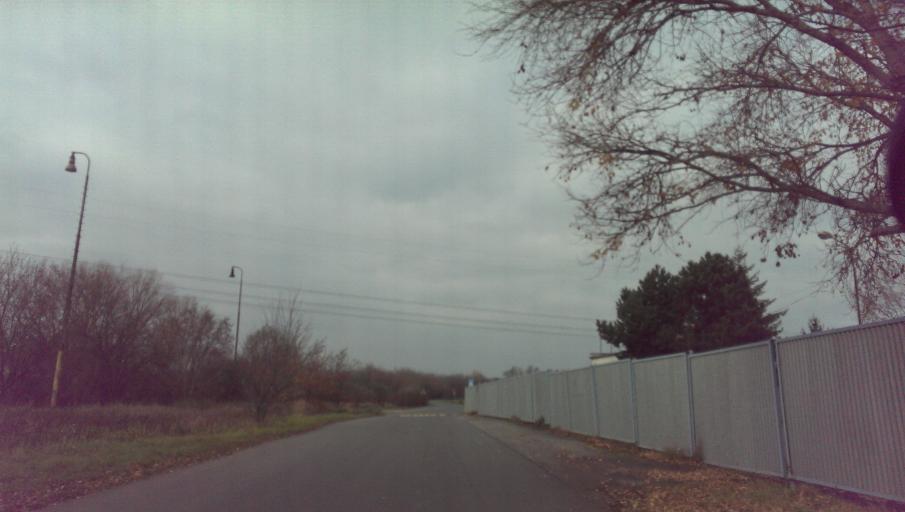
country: CZ
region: Zlin
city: Tlumacov
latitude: 49.2641
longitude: 17.4950
